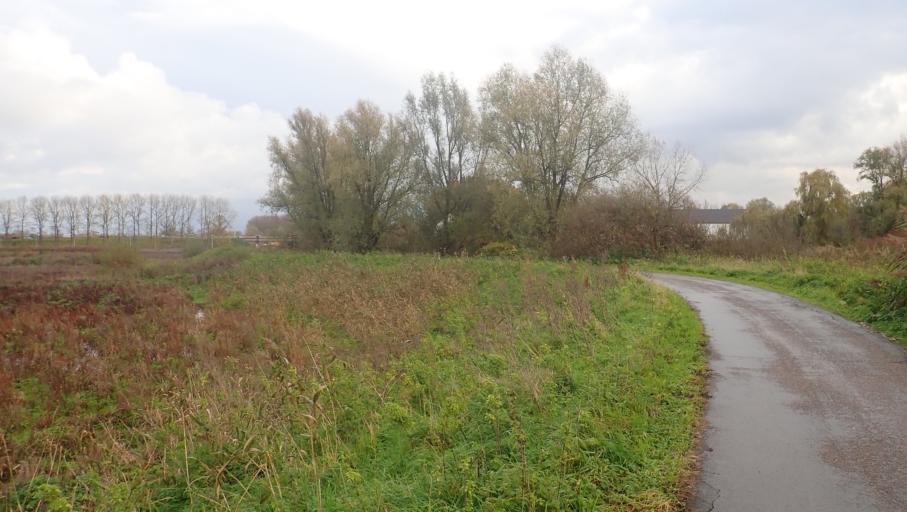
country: BE
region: Flanders
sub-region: Provincie Oost-Vlaanderen
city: Hamme
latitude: 51.1056
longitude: 4.1375
